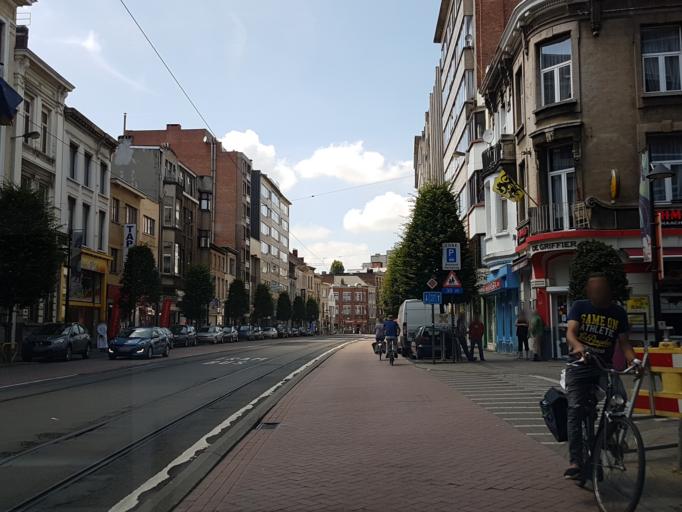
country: BE
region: Flanders
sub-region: Provincie Antwerpen
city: Antwerpen
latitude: 51.2155
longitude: 4.4324
